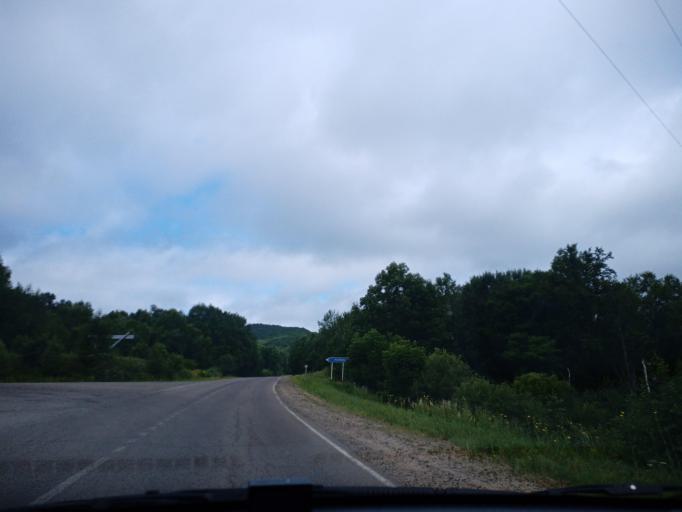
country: RU
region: Primorskiy
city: Novopokrovka
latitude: 45.8421
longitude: 134.4479
